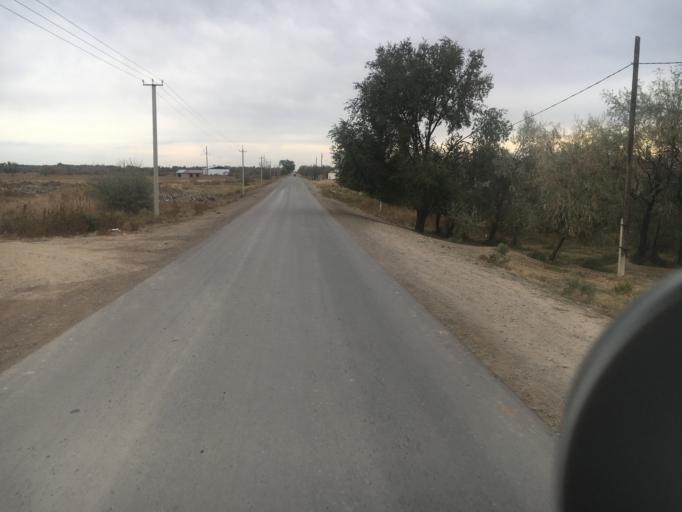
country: KZ
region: Almaty Oblysy
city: Energeticheskiy
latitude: 43.5860
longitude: 77.0650
